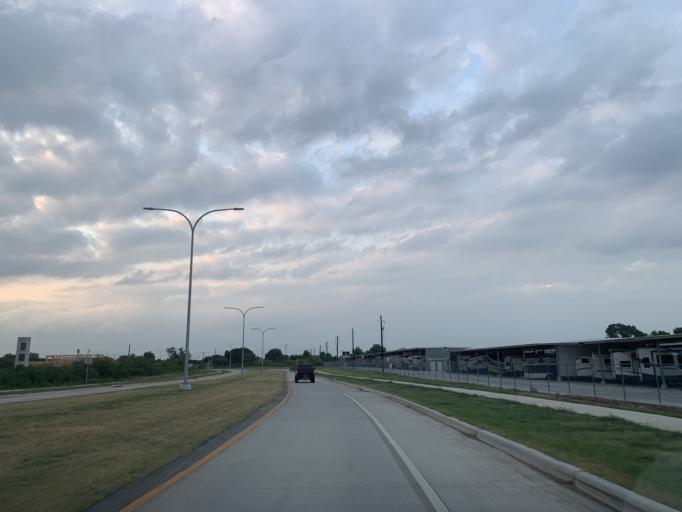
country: US
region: Texas
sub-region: Tarrant County
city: Keller
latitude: 32.9349
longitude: -97.2715
